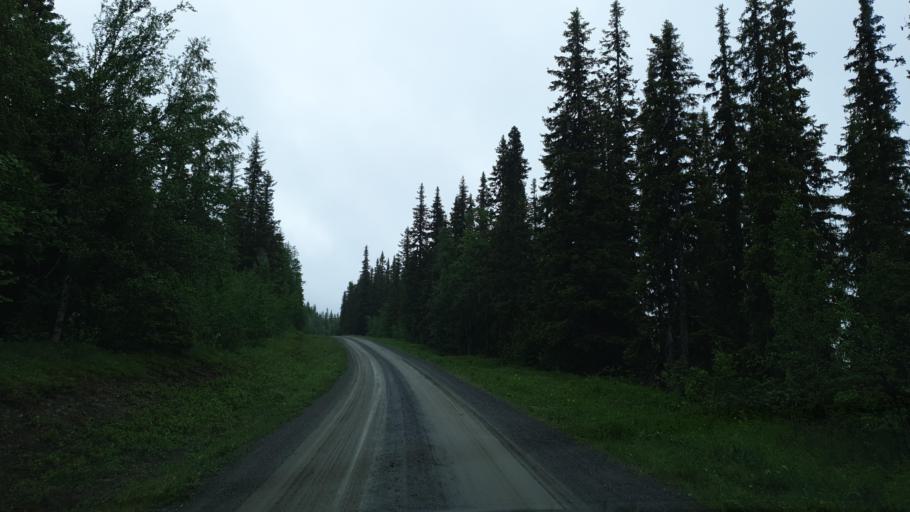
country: SE
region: Vaesterbotten
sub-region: Vilhelmina Kommun
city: Sjoberg
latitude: 65.3308
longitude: 15.9090
